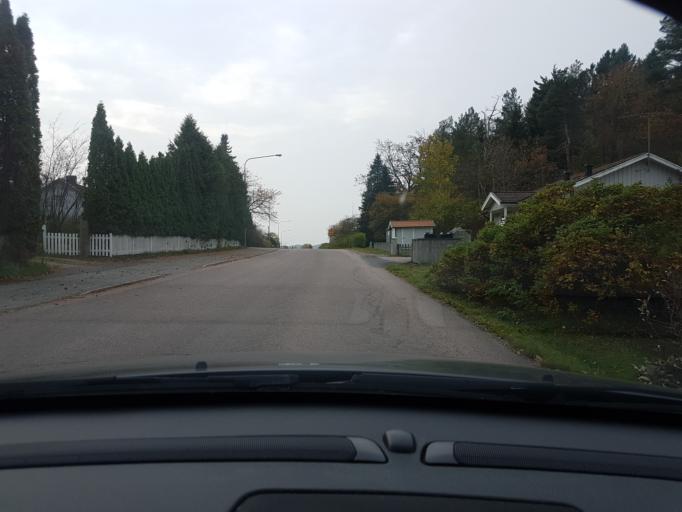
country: SE
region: Vaestra Goetaland
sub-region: Ale Kommun
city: Alvangen
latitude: 57.9520
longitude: 12.1100
